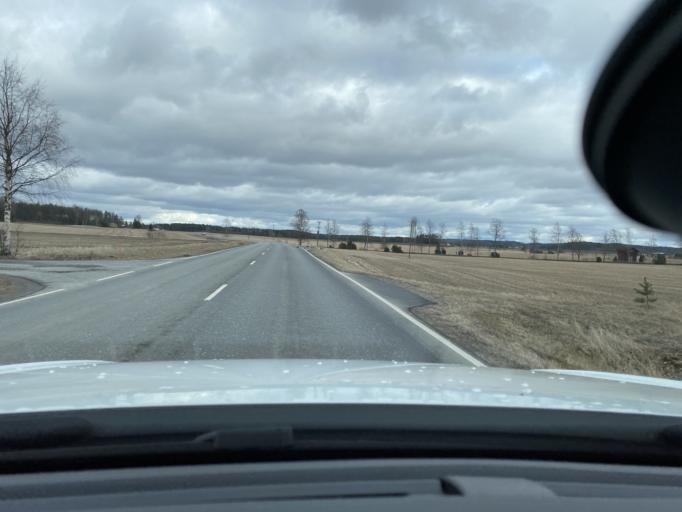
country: FI
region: Pirkanmaa
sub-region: Lounais-Pirkanmaa
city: Punkalaidun
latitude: 61.1035
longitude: 23.1512
